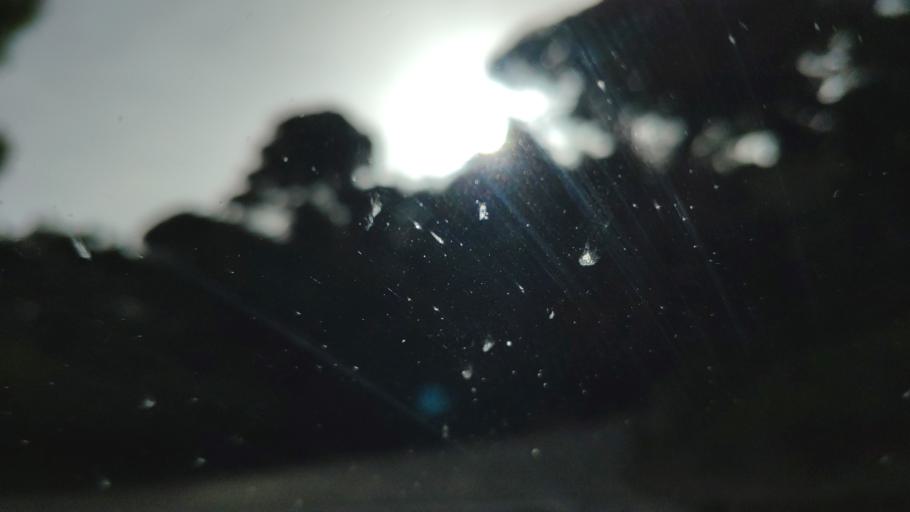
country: GR
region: Attica
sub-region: Nomarchia Anatolikis Attikis
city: Limin Mesoyaias
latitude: 37.8475
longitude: 24.0279
